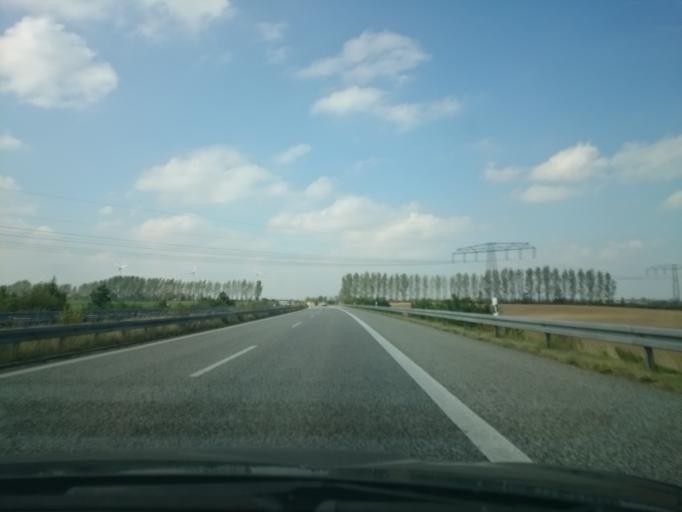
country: DE
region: Brandenburg
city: Schonfeld
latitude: 53.4451
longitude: 13.9875
